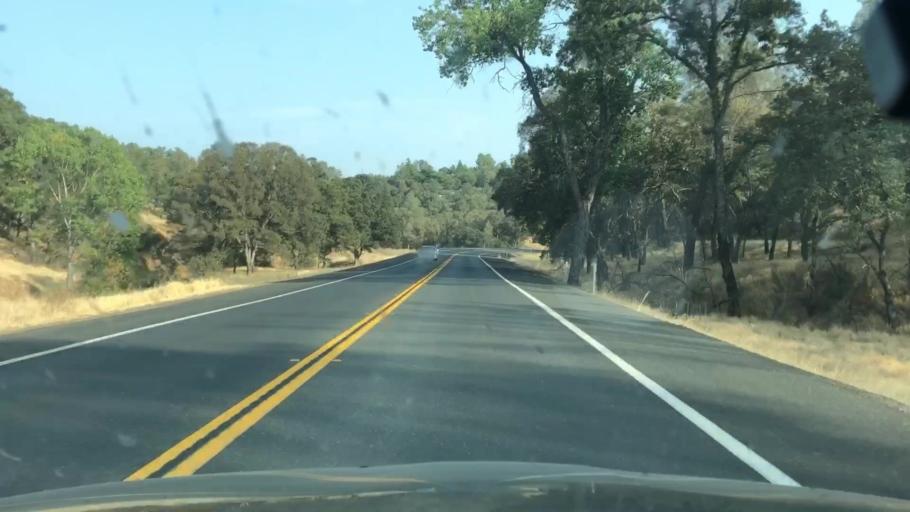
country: US
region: California
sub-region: Lake County
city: Hidden Valley Lake
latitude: 38.8167
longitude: -122.5739
